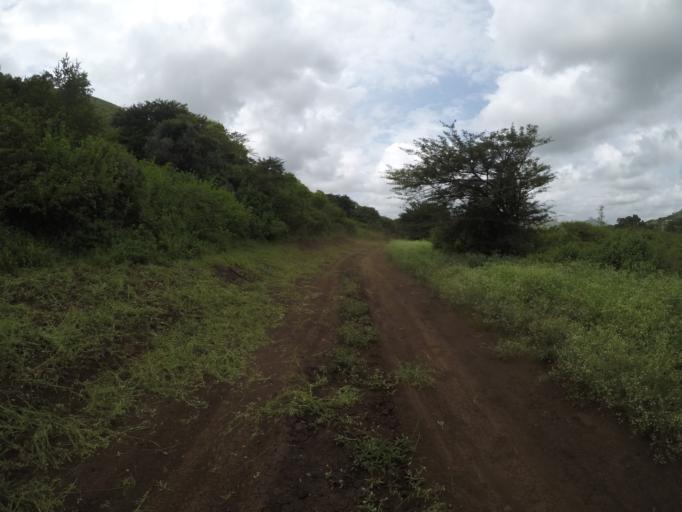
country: ZA
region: KwaZulu-Natal
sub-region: uThungulu District Municipality
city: Empangeni
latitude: -28.5891
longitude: 31.8721
